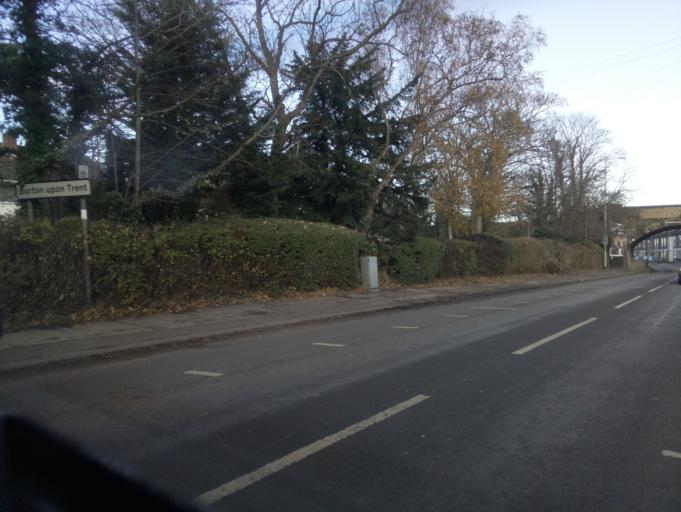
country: GB
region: England
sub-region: Staffordshire
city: Burton upon Trent
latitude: 52.7903
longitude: -1.6453
